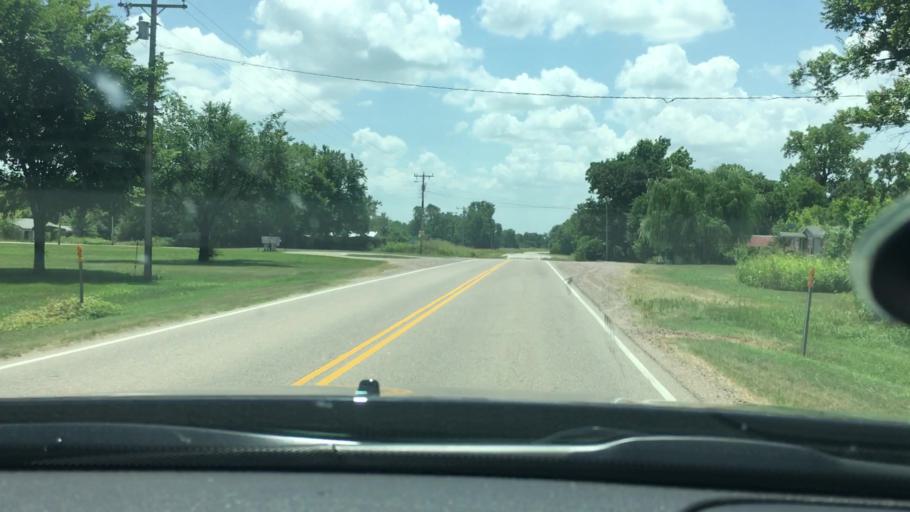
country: US
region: Oklahoma
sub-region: Johnston County
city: Tishomingo
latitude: 34.4897
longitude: -96.6271
